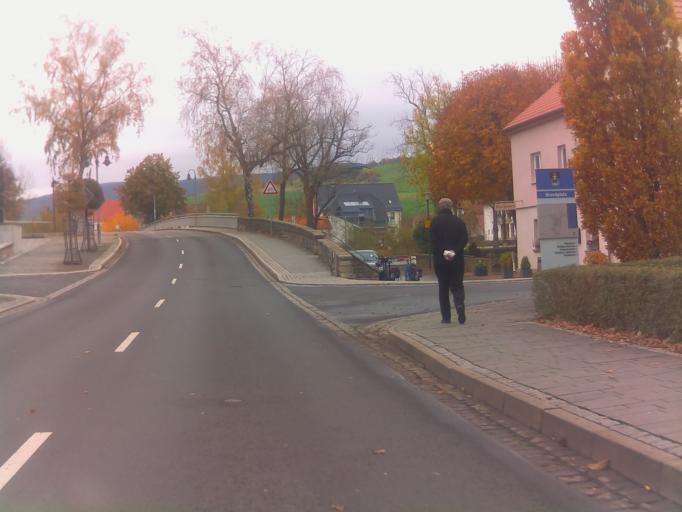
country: DE
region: Thuringia
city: Geisa
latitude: 50.7168
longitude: 9.9512
